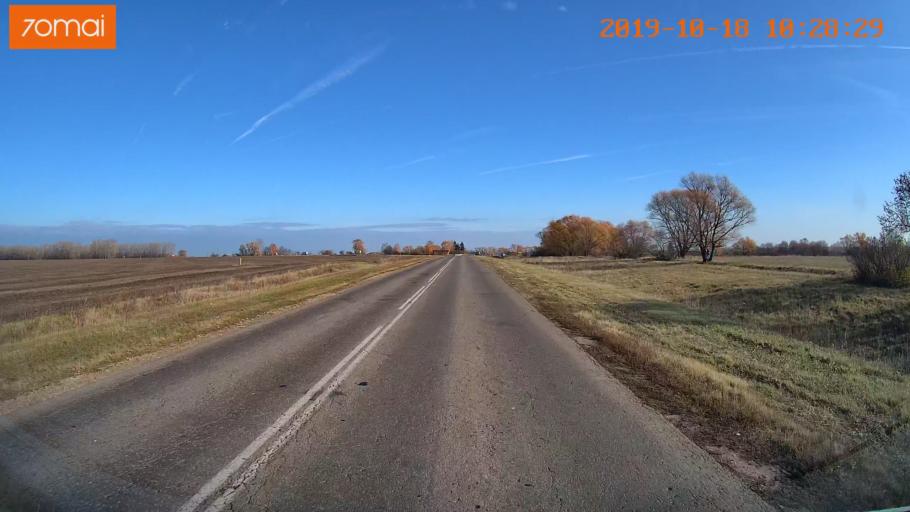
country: RU
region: Tula
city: Kurkino
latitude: 53.4445
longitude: 38.6559
